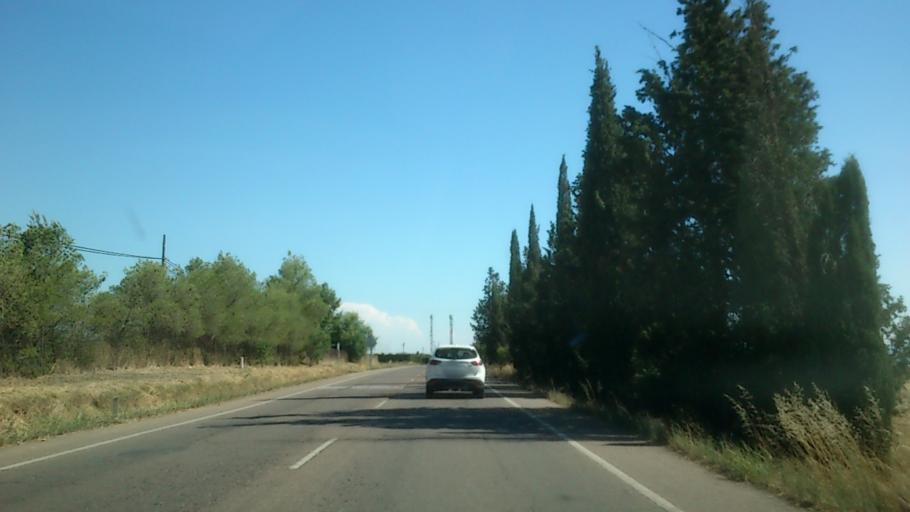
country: ES
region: Aragon
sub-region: Provincia de Zaragoza
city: Villanueva de Gallego
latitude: 41.7215
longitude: -0.8105
